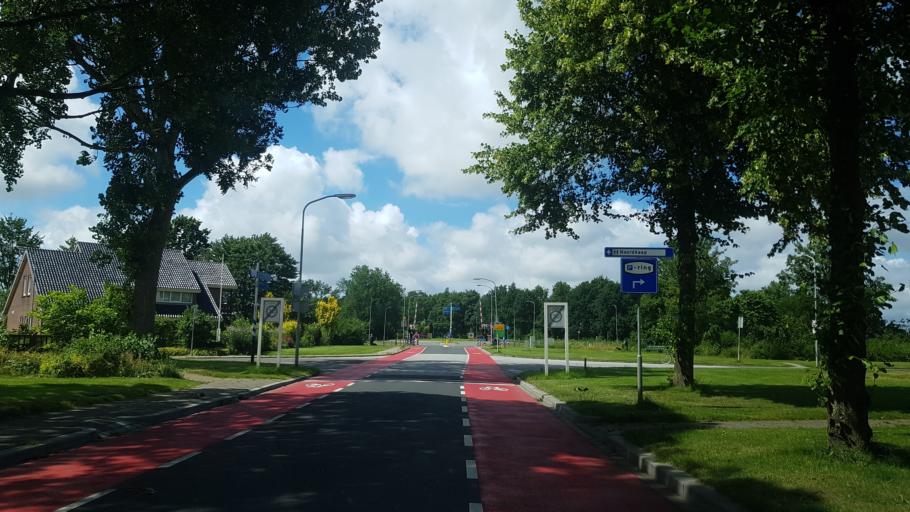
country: NL
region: Groningen
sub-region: Gemeente Bedum
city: Bedum
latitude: 53.4068
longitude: 6.6616
